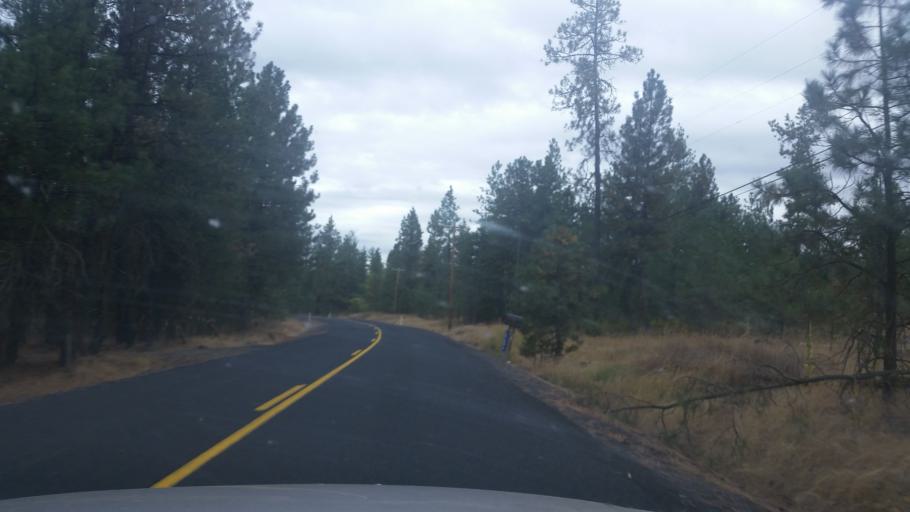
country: US
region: Washington
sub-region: Spokane County
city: Medical Lake
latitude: 47.5005
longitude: -117.7719
